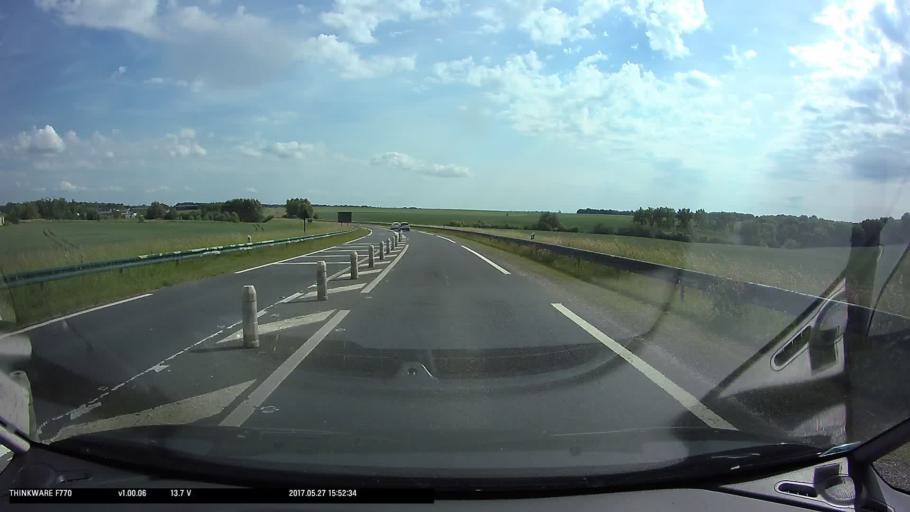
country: FR
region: Ile-de-France
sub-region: Departement du Val-d'Oise
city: Marines
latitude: 49.1503
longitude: 1.9640
